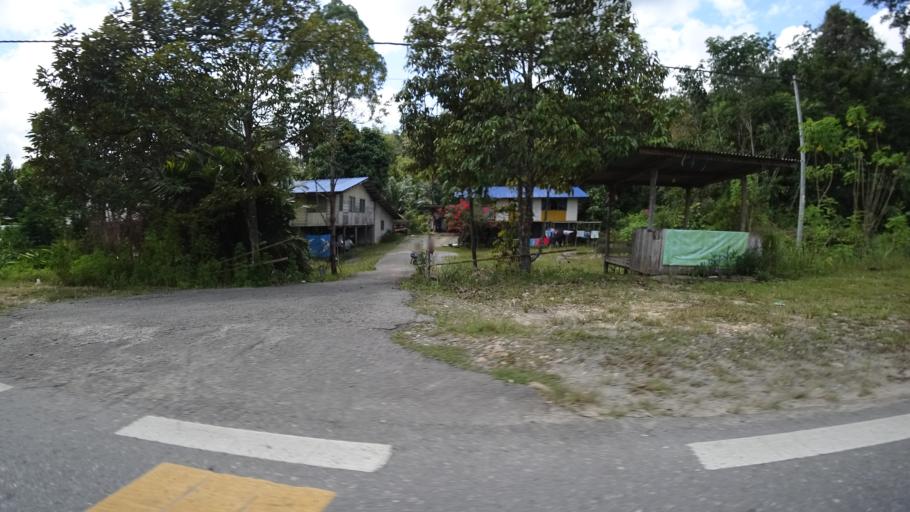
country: MY
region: Sarawak
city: Limbang
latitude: 4.6593
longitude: 114.9534
